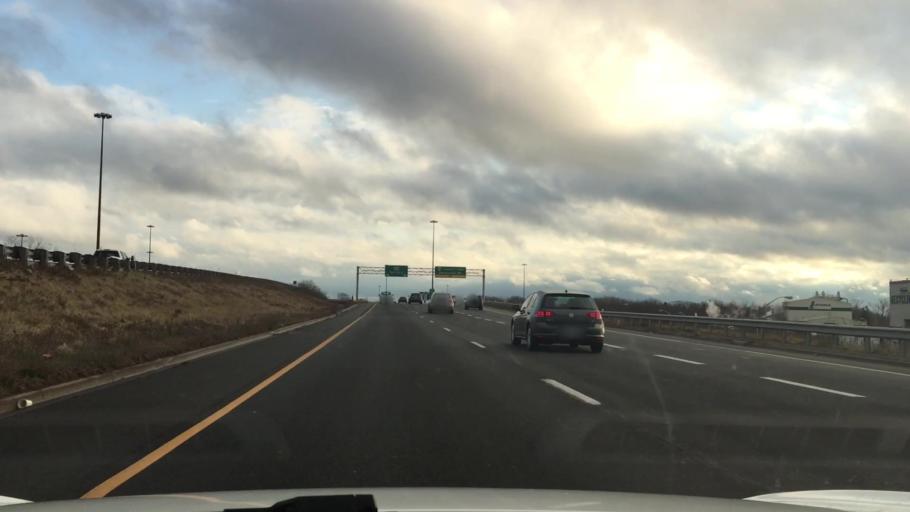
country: CA
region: Ontario
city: Niagara Falls
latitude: 43.1019
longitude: -79.1196
